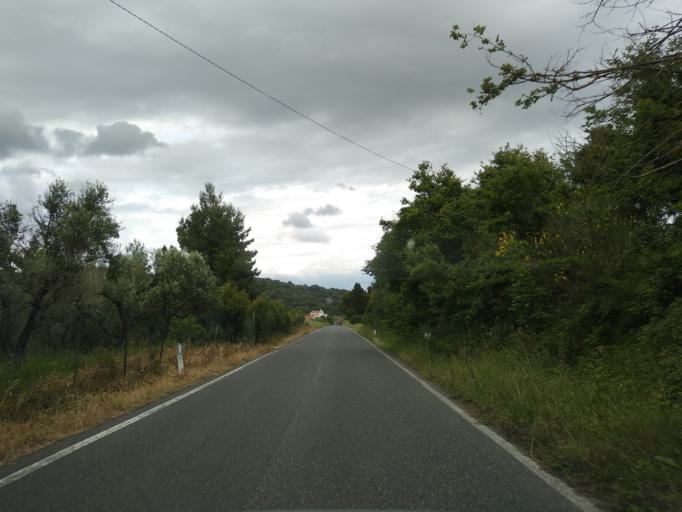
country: IT
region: Tuscany
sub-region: Provincia di Livorno
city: Collesalvetti
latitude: 43.5405
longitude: 10.4485
